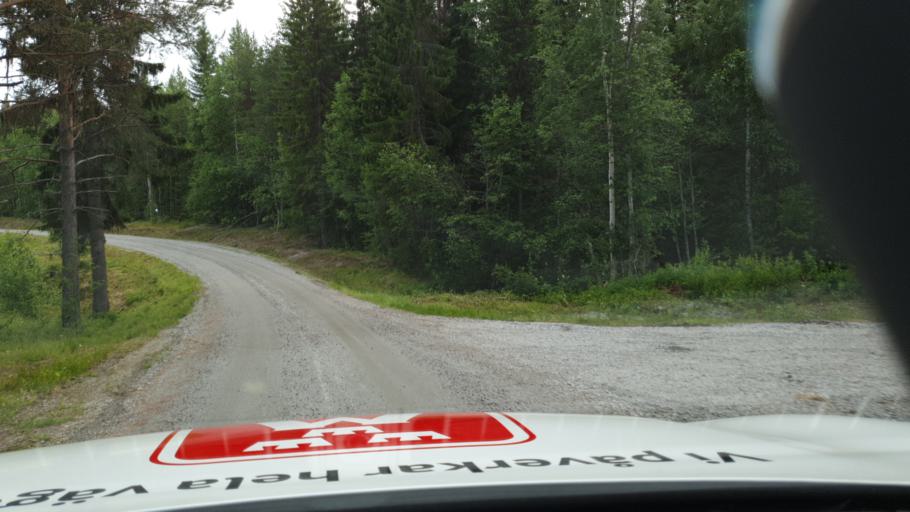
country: SE
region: Vaesterbotten
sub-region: Dorotea Kommun
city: Dorotea
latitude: 63.8519
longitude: 16.3364
